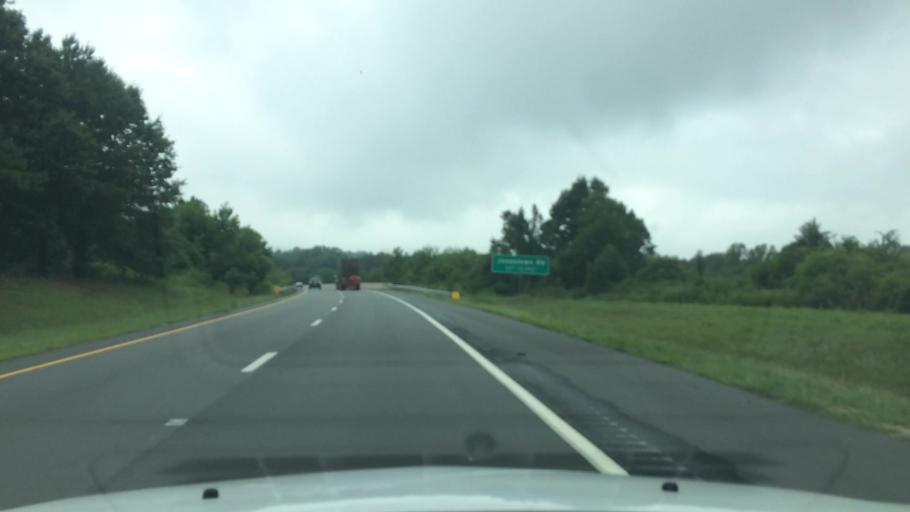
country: US
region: North Carolina
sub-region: Forsyth County
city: Clemmons
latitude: 36.0721
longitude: -80.3231
